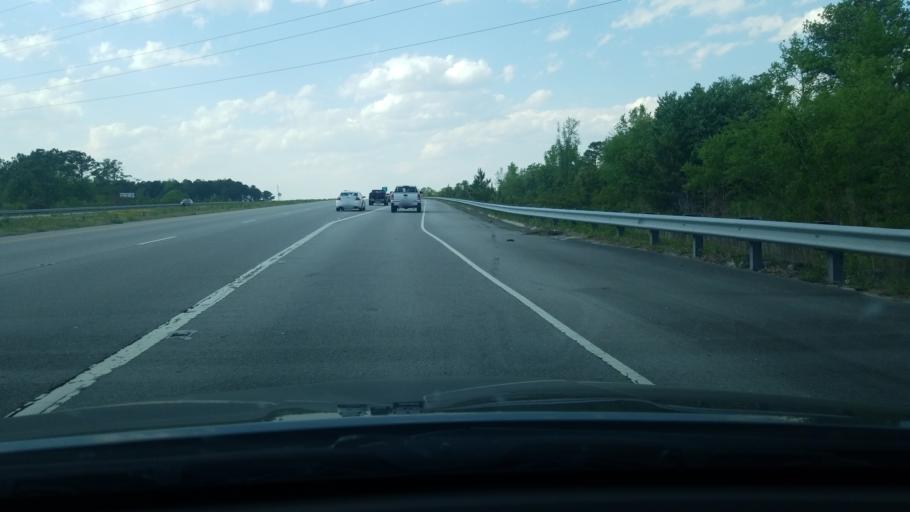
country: US
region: North Carolina
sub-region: Onslow County
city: Pumpkin Center
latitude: 34.7654
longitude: -77.3955
